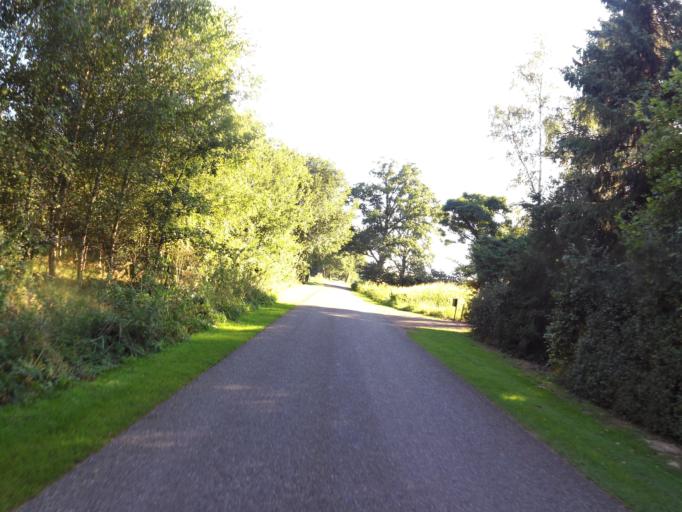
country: NL
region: Gelderland
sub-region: Gemeente Winterswijk
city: Winterswijk
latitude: 51.9277
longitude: 6.7575
